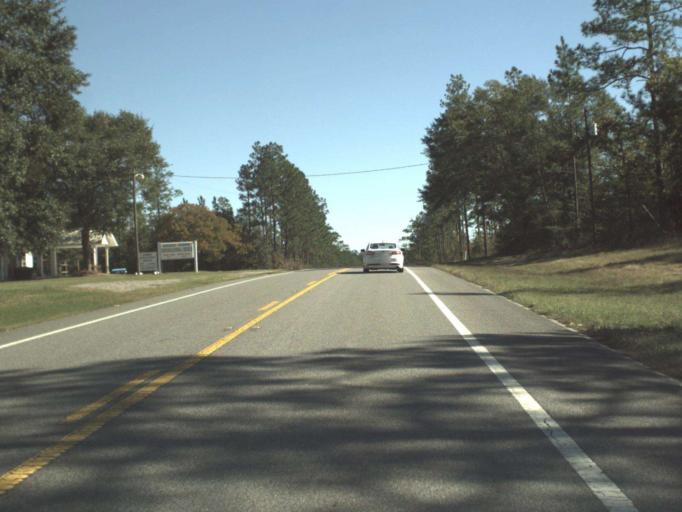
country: US
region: Florida
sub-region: Okaloosa County
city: Crestview
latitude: 30.8503
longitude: -86.7762
